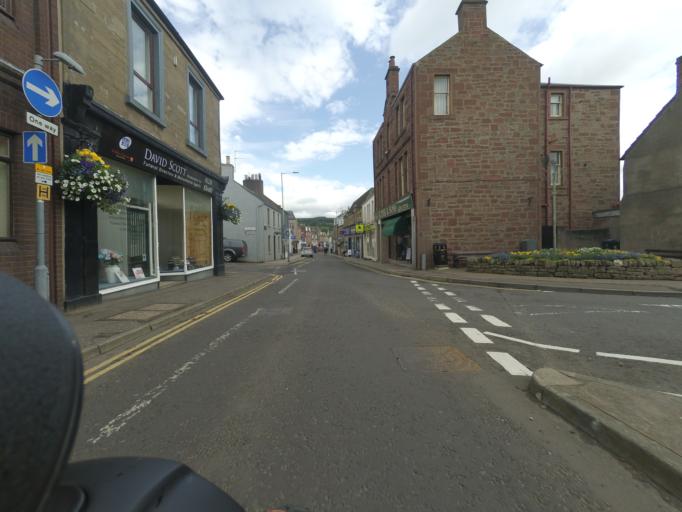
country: GB
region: Scotland
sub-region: Perth and Kinross
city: Blairgowrie
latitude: 56.5914
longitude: -3.3406
